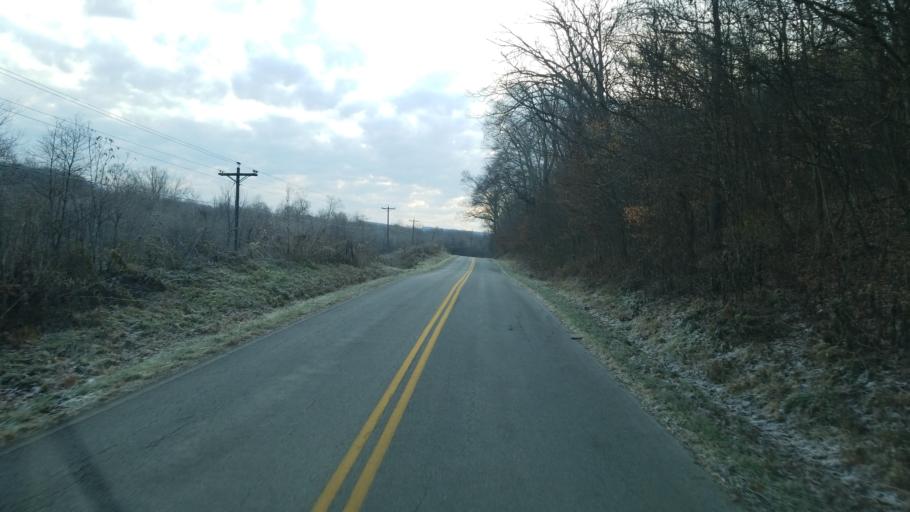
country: US
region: Ohio
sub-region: Pike County
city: Waverly
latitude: 39.2276
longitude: -82.8833
